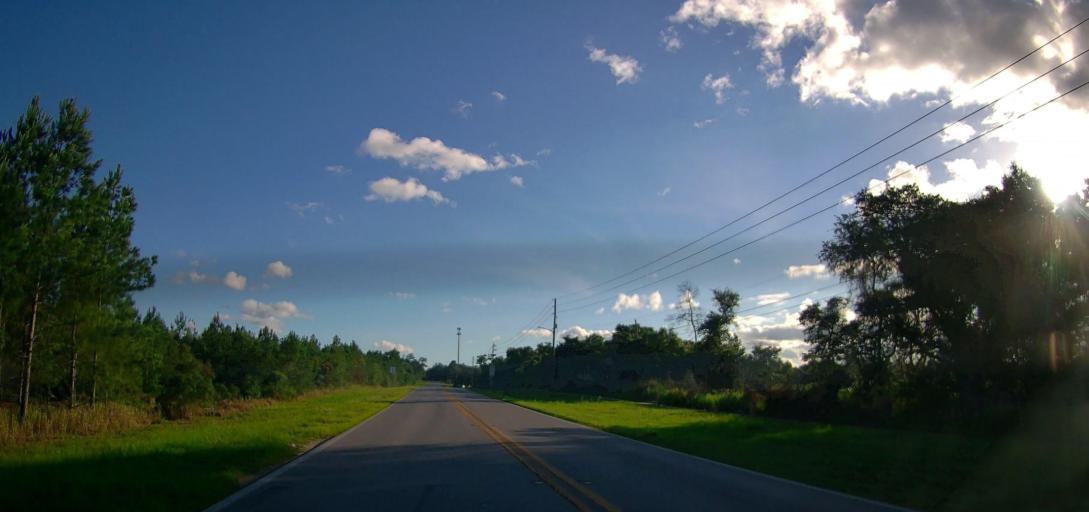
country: US
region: Florida
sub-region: Marion County
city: Silver Springs Shores
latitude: 29.0840
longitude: -82.0021
